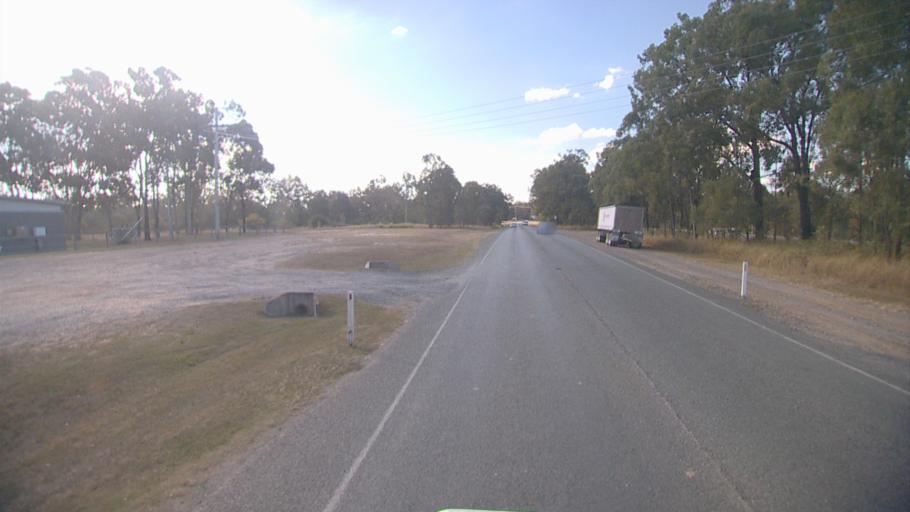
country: AU
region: Queensland
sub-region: Logan
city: Park Ridge South
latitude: -27.7281
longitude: 152.9841
